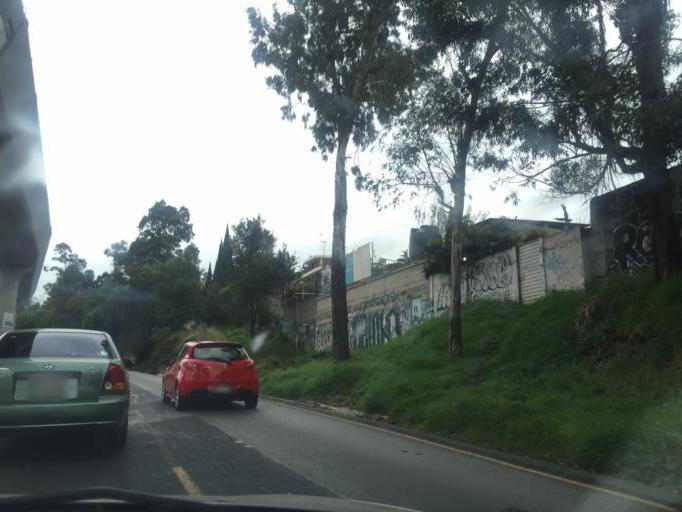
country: MX
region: Mexico City
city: Xochimilco
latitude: 19.2472
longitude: -99.1539
